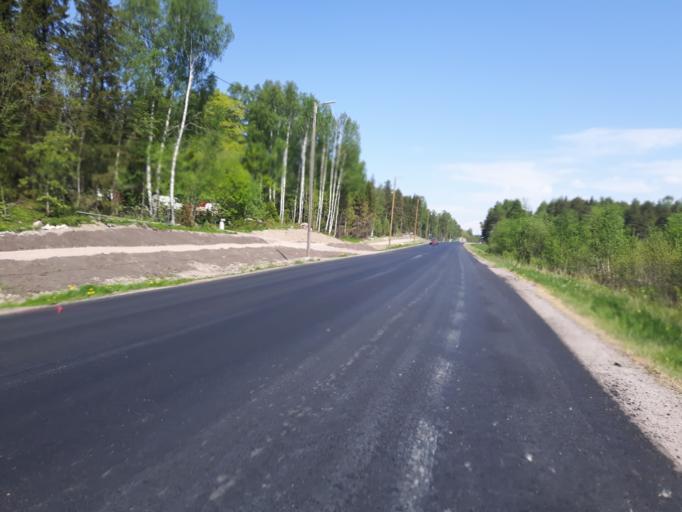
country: FI
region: Uusimaa
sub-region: Porvoo
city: Porvoo
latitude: 60.3594
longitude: 25.5361
